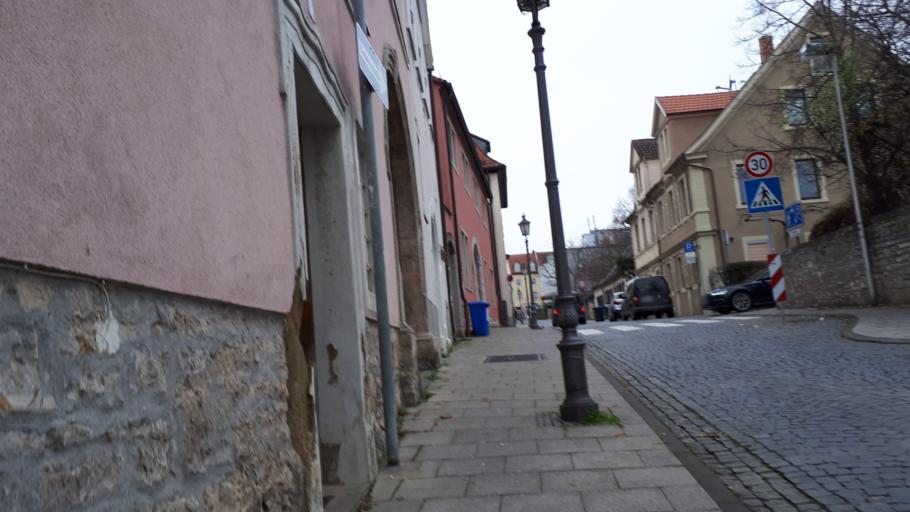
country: DE
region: Bavaria
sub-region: Regierungsbezirk Unterfranken
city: Kitzingen
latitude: 49.7366
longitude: 10.1636
